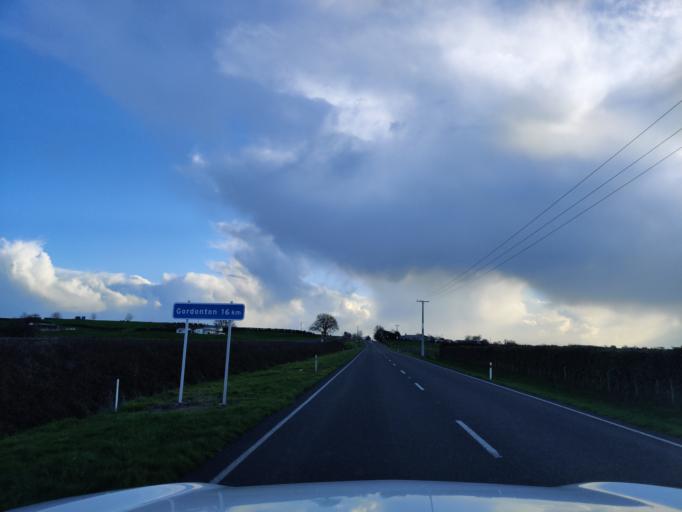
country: NZ
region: Waikato
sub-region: Waipa District
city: Cambridge
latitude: -37.6690
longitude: 175.4798
